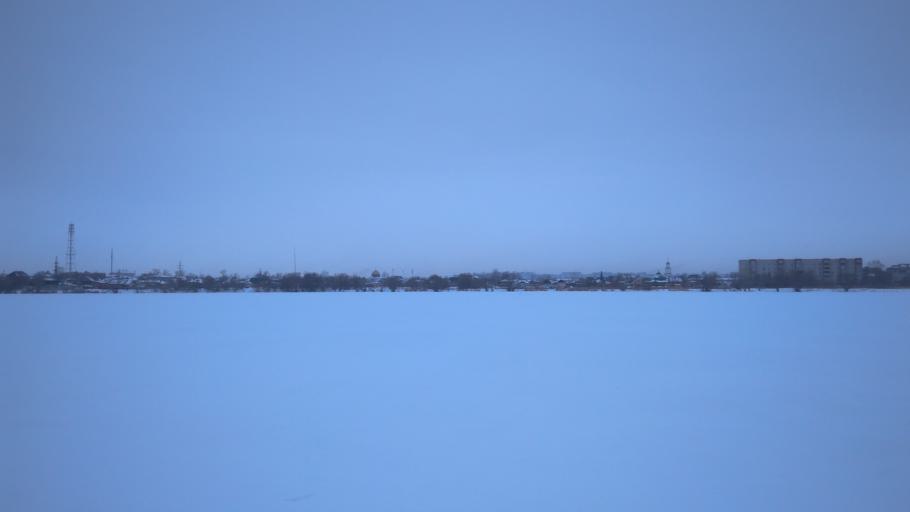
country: RU
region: Chelyabinsk
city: Troitsk
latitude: 54.0788
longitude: 61.5757
